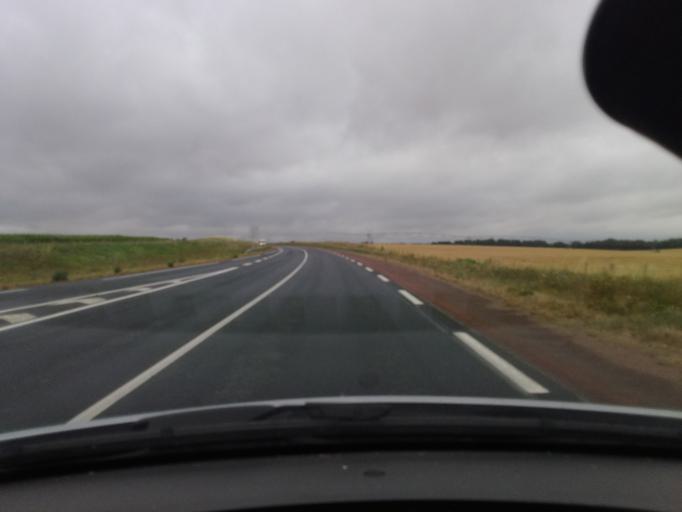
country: FR
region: Pays de la Loire
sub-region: Departement de la Vendee
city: Lucon
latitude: 46.4699
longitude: -1.1567
